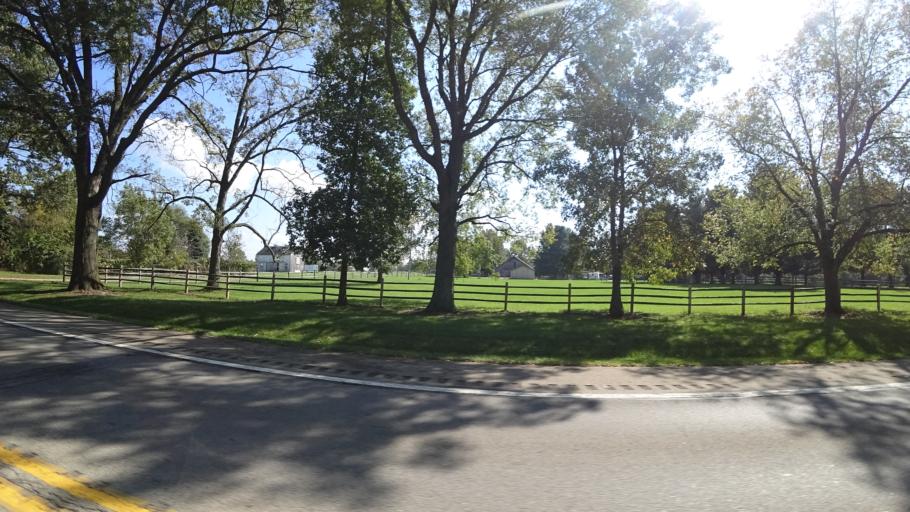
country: US
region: Michigan
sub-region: Calhoun County
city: Homer
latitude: 42.1543
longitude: -84.7834
